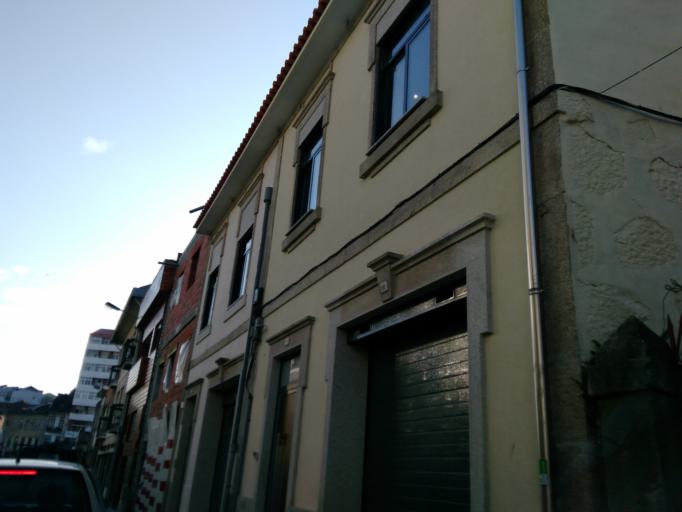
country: PT
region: Porto
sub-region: Porto
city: Porto
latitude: 41.1515
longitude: -8.5904
